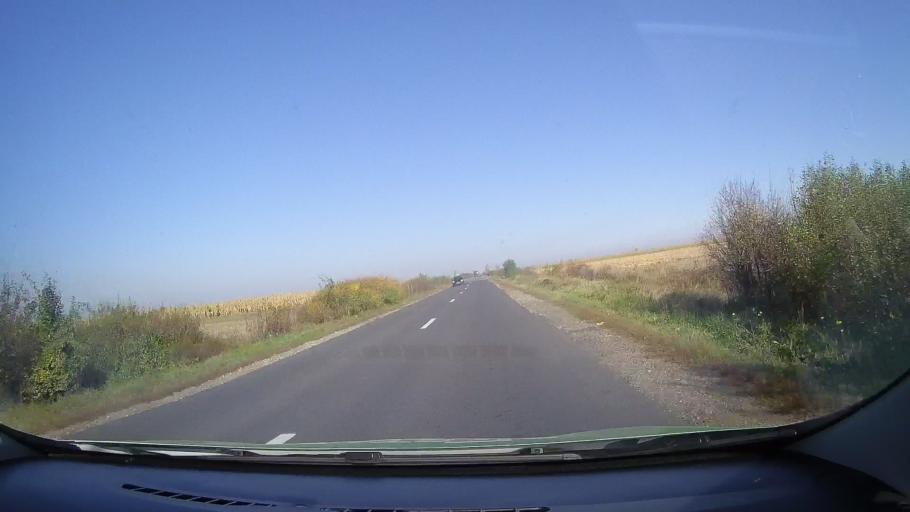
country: RO
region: Satu Mare
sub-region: Oras Tasnad
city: Tasnad
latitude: 47.5189
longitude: 22.5710
